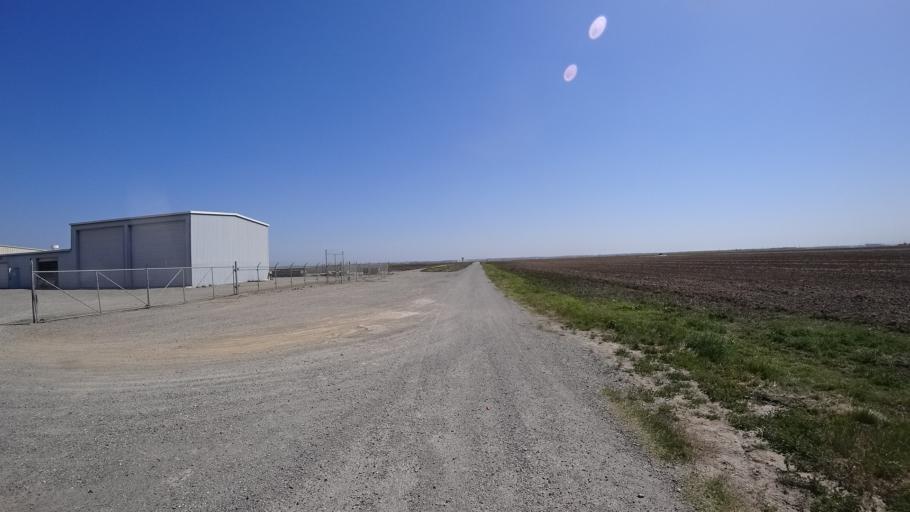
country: US
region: California
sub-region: Glenn County
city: Willows
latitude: 39.5291
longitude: -122.0744
